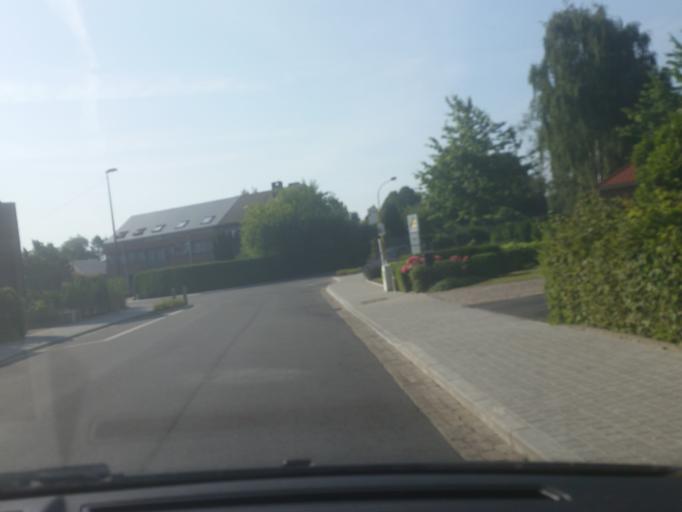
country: BE
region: Flanders
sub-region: Provincie Antwerpen
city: Mechelen
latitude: 51.0065
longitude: 4.4688
